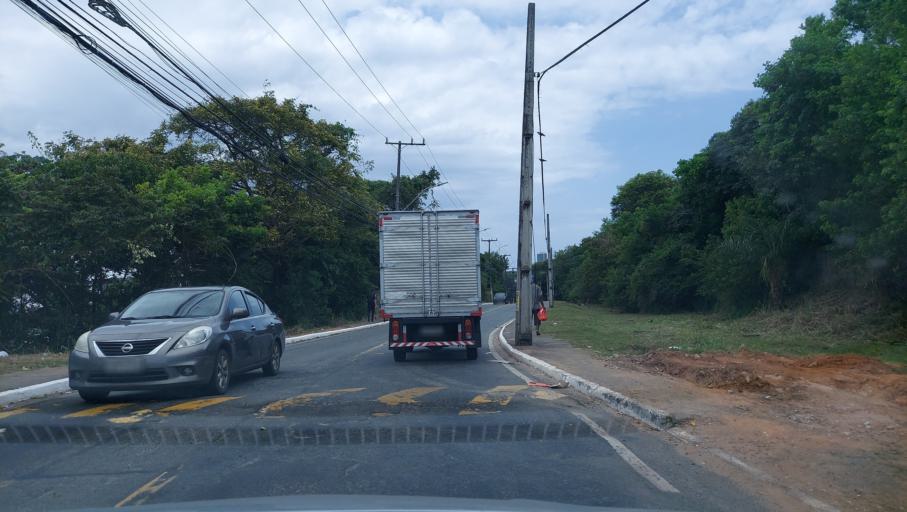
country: BR
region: Bahia
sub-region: Salvador
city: Salvador
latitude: -12.9659
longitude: -38.4430
